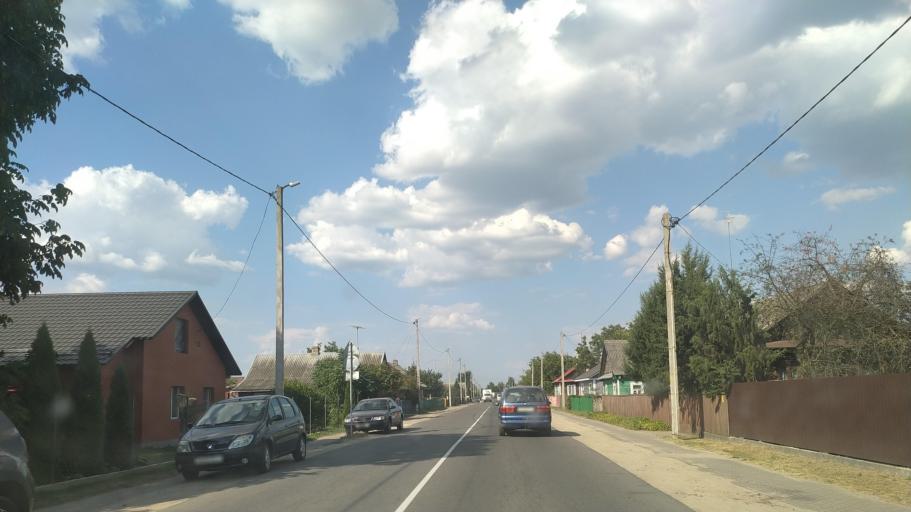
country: BY
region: Brest
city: Drahichyn
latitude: 52.1949
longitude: 25.1476
